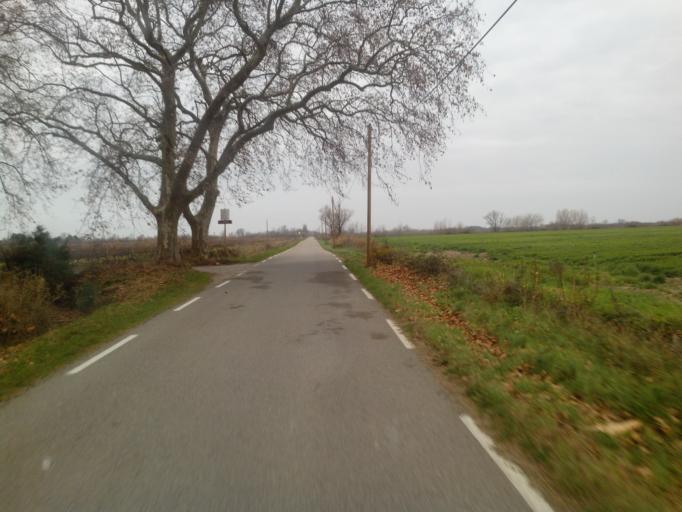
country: FR
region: Languedoc-Roussillon
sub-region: Departement du Gard
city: Vauvert
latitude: 43.5753
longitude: 4.3316
